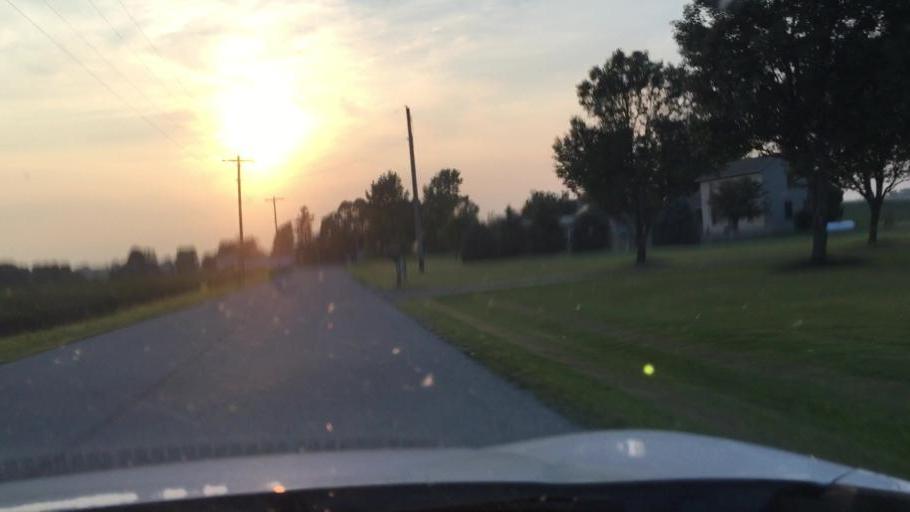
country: US
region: Ohio
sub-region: Madison County
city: Choctaw Lake
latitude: 39.9482
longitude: -83.5637
